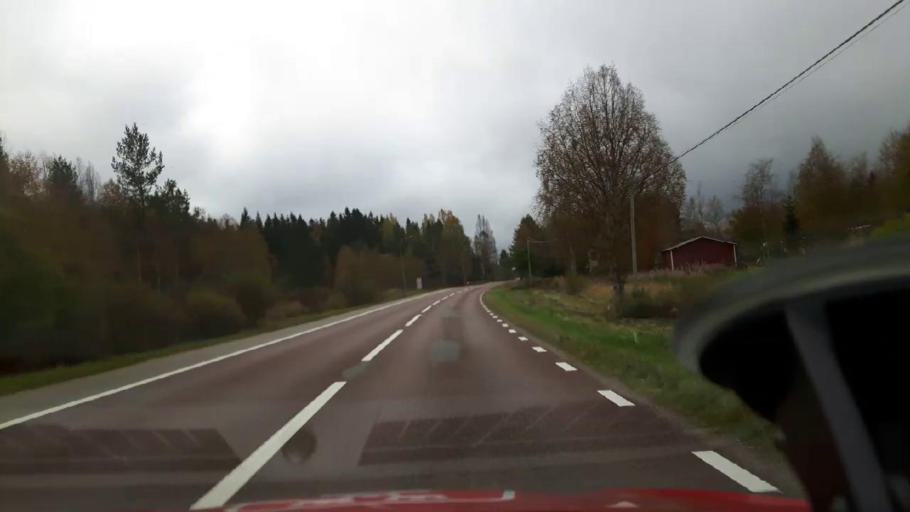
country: SE
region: Jaemtland
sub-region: Harjedalens Kommun
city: Sveg
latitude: 62.2924
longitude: 14.7907
